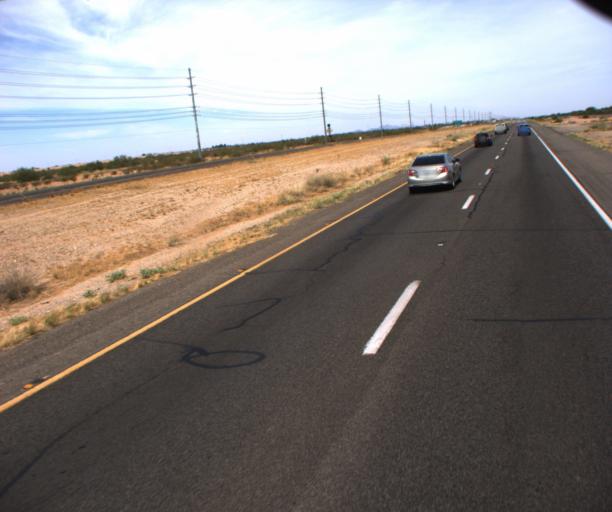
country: US
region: Arizona
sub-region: Maricopa County
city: Sun City West
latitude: 33.6881
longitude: -112.4134
